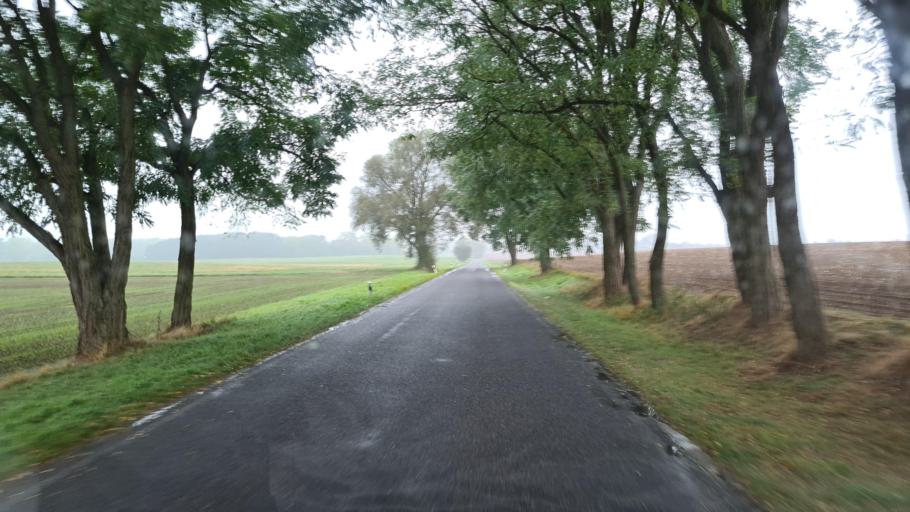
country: DE
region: Brandenburg
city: Furstenwalde
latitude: 52.4299
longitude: 14.0307
